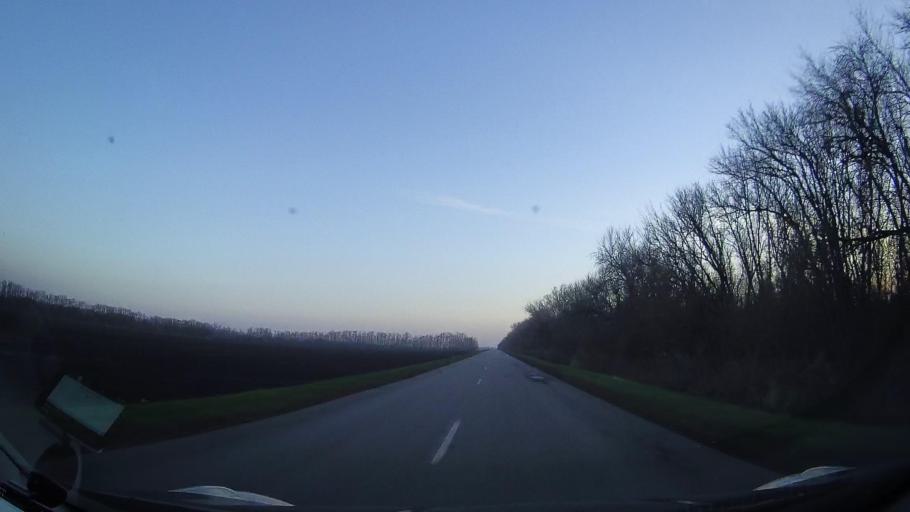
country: RU
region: Rostov
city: Zernograd
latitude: 46.9944
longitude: 40.3915
